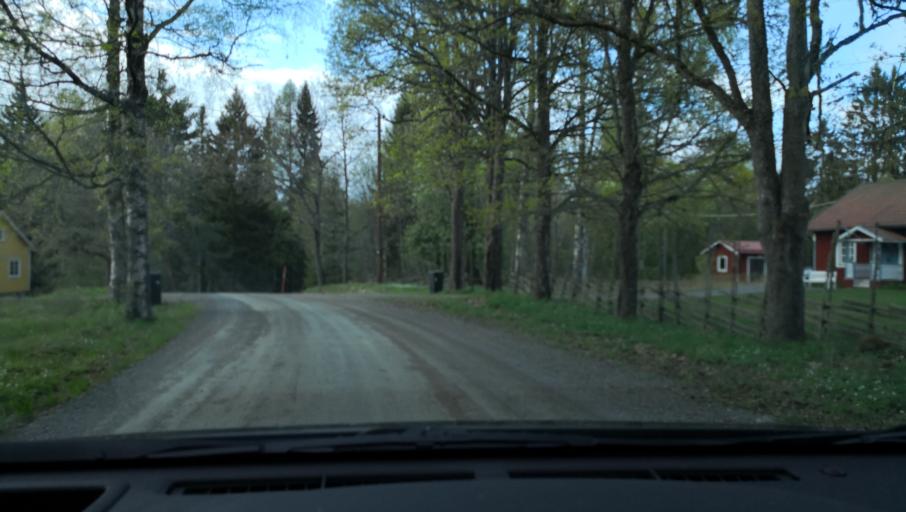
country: SE
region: Dalarna
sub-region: Saters Kommun
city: Saeter
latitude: 60.2658
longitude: 15.8278
